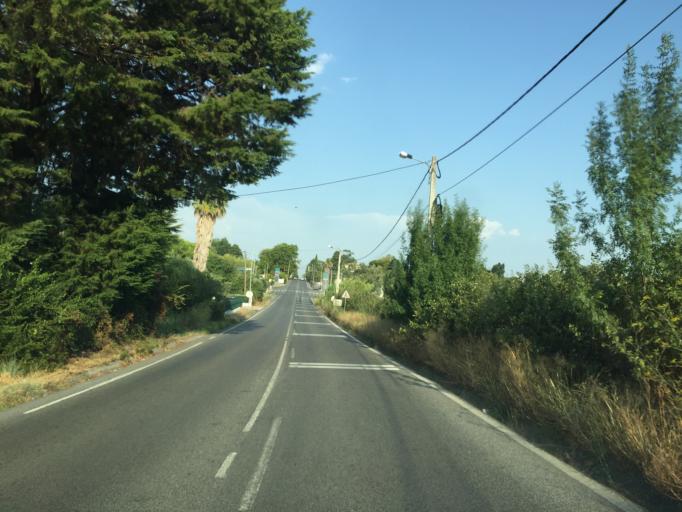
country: PT
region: Santarem
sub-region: Torres Novas
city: Torres Novas
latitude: 39.4769
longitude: -8.5675
